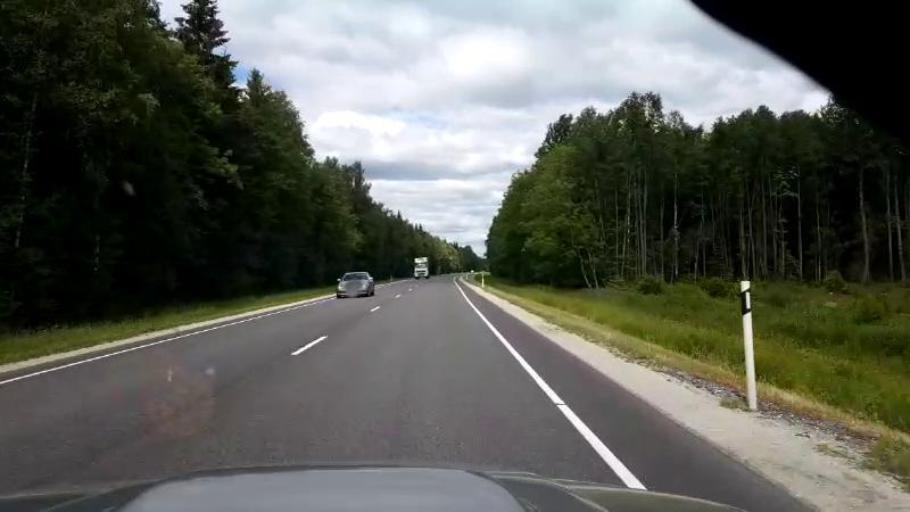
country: EE
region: Raplamaa
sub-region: Maerjamaa vald
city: Marjamaa
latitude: 58.8258
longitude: 24.4151
